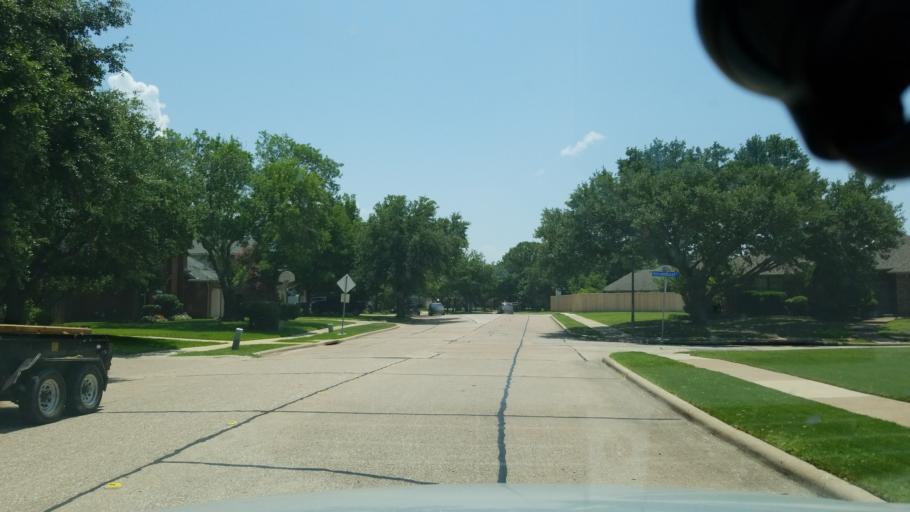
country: US
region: Texas
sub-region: Dallas County
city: Coppell
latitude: 32.9626
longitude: -96.9971
